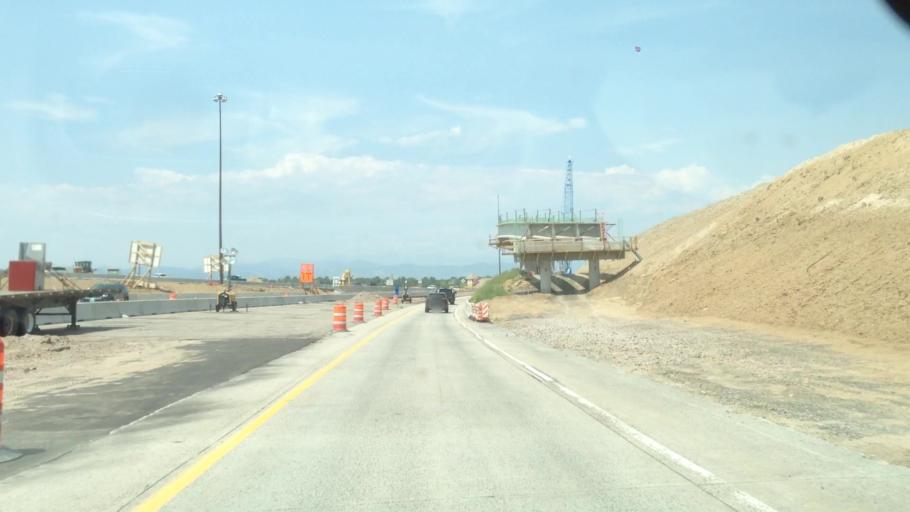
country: US
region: Colorado
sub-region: Adams County
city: Lone Tree
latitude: 39.5556
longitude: -104.8732
